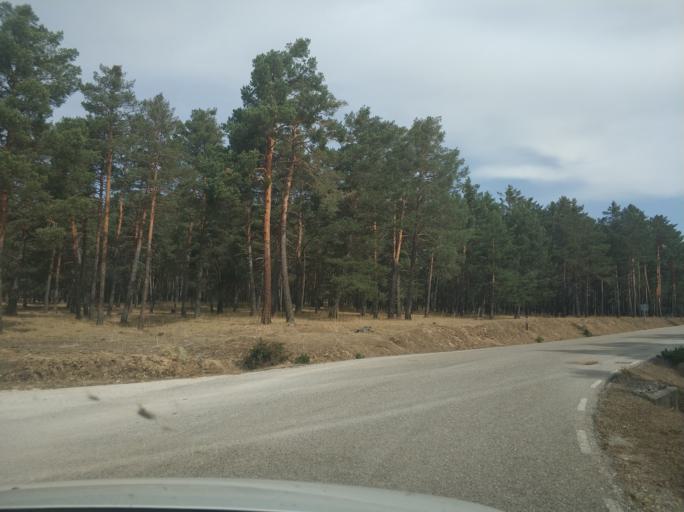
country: ES
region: Castille and Leon
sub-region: Provincia de Soria
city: Navaleno
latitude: 41.8678
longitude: -2.9452
